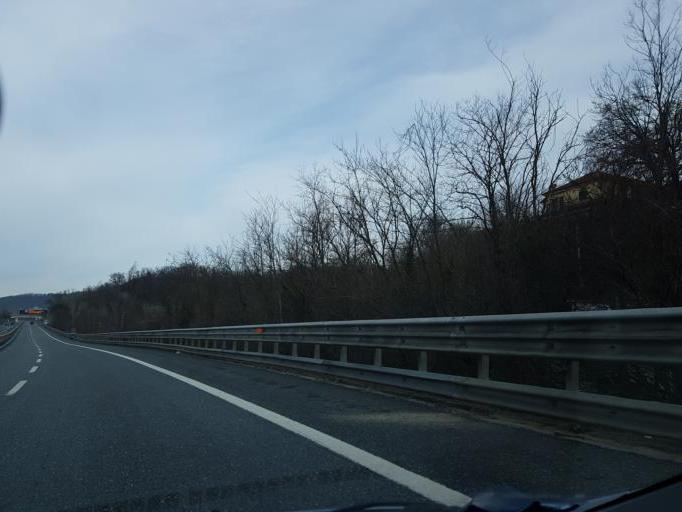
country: IT
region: Piedmont
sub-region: Provincia di Alessandria
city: Arquata Scrivia
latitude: 44.6905
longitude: 8.9004
